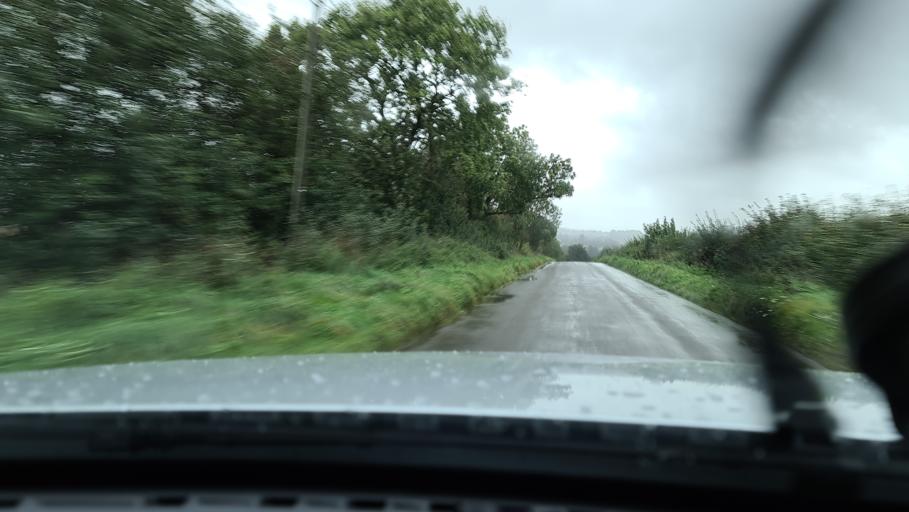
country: GB
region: England
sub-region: Oxfordshire
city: Deddington
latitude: 51.9219
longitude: -1.3673
